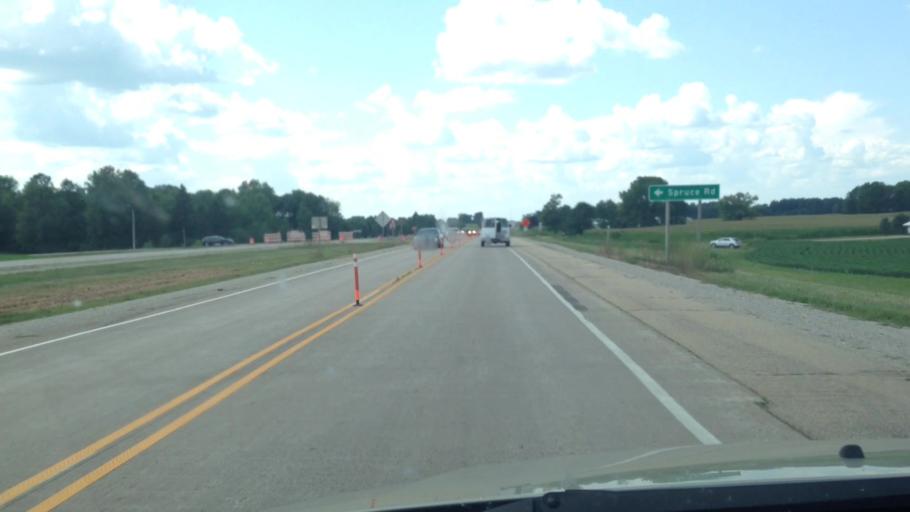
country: US
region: Wisconsin
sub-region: Brown County
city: Pulaski
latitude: 44.6931
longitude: -88.3374
